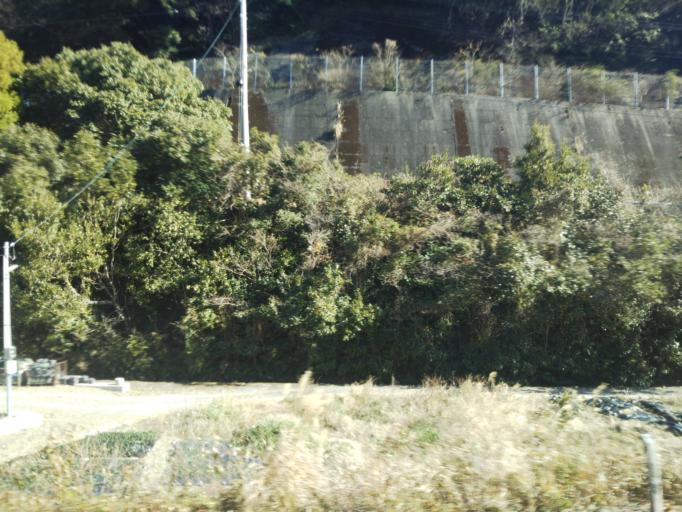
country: JP
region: Kochi
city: Nakamura
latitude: 33.0823
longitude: 133.1017
